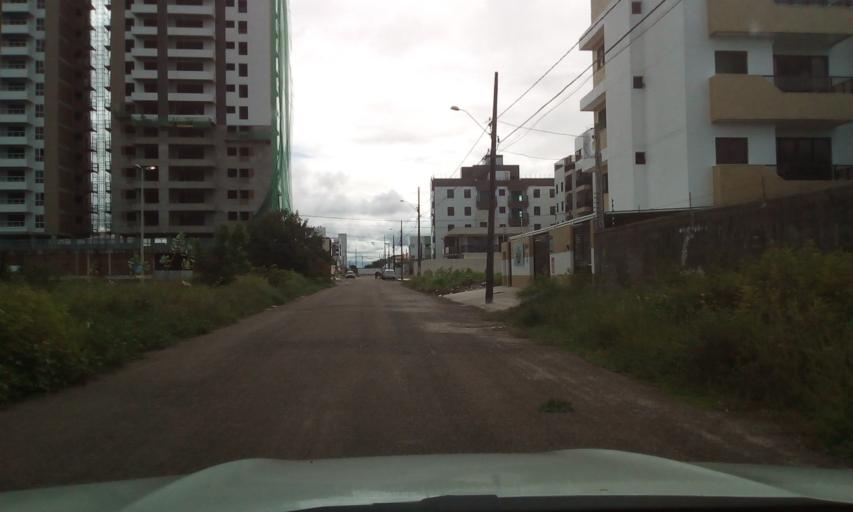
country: BR
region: Paraiba
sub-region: Joao Pessoa
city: Joao Pessoa
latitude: -7.0526
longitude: -34.8464
